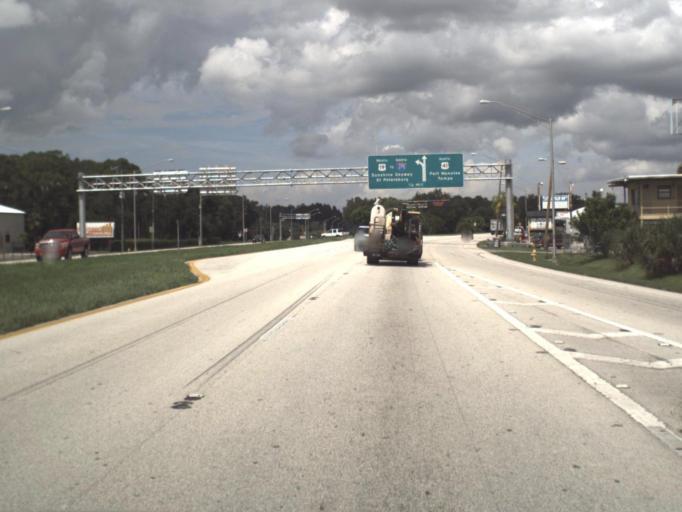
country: US
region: Florida
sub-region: Manatee County
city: Memphis
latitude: 27.5444
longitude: -82.5644
